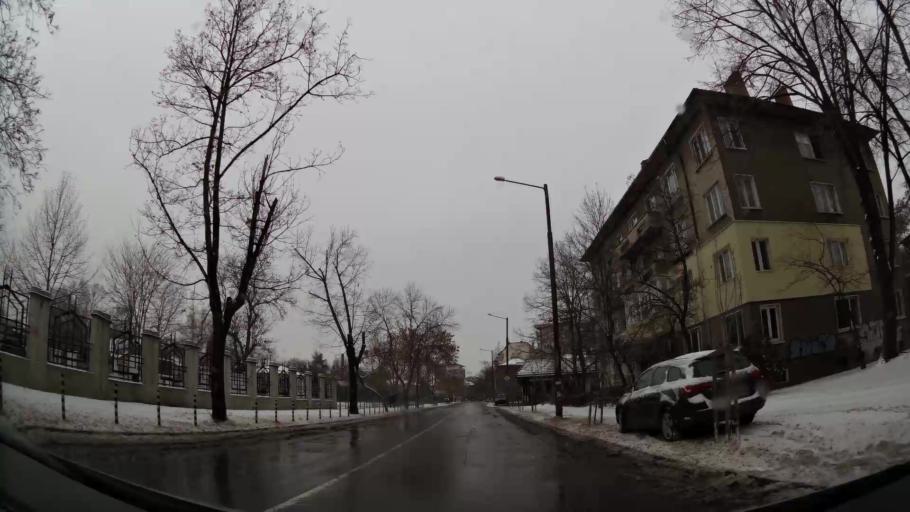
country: BG
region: Sofia-Capital
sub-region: Stolichna Obshtina
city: Sofia
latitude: 42.6893
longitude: 23.3515
